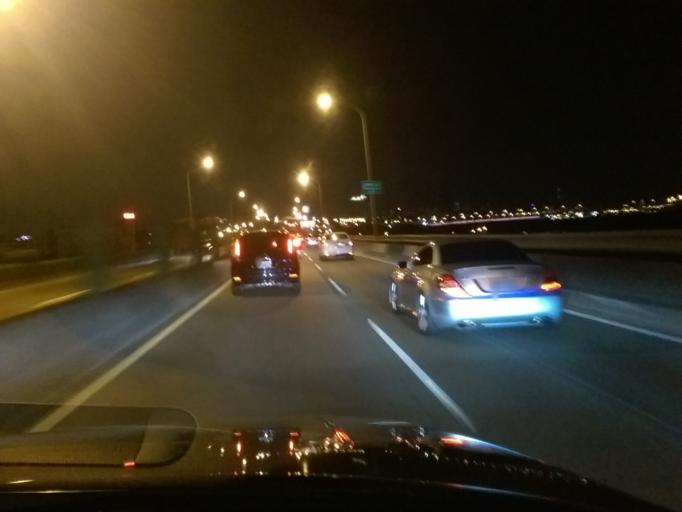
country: TW
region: Taipei
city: Taipei
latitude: 25.0406
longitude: 121.4979
